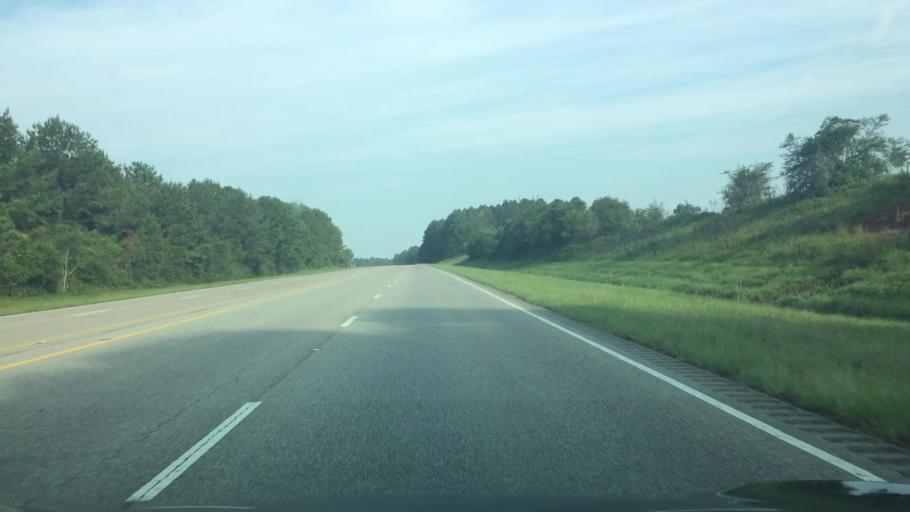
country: US
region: Alabama
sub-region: Covington County
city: Andalusia
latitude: 31.4014
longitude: -86.5866
